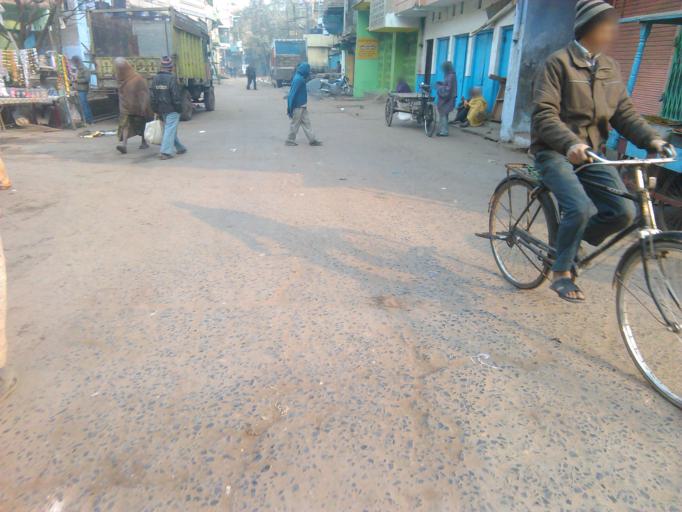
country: IN
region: Bihar
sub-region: Gaya
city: Gaya
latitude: 24.7980
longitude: 85.0039
